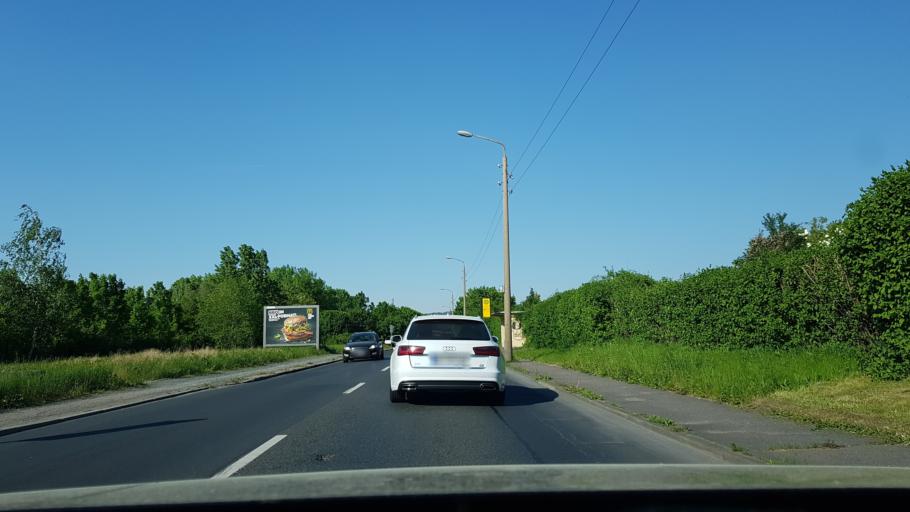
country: DE
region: Saxony
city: Heidenau
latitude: 51.0012
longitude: 13.8024
